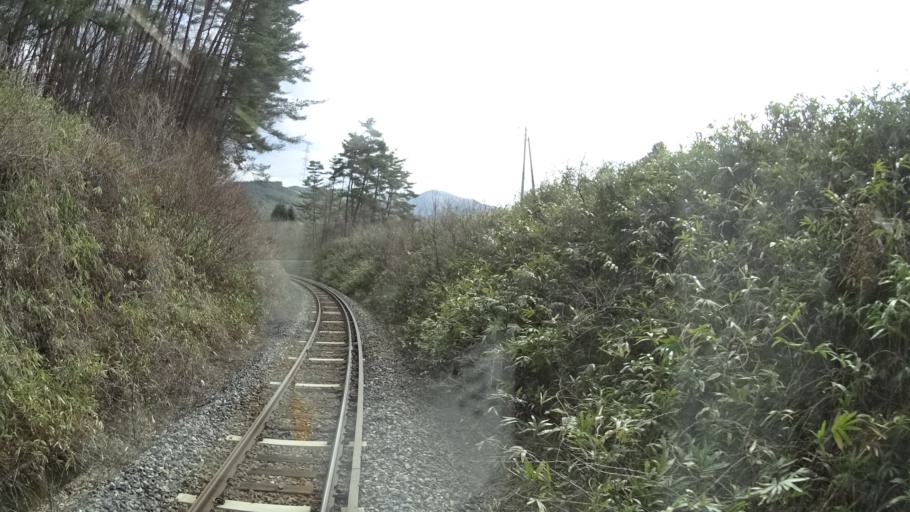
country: JP
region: Iwate
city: Tono
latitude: 39.3390
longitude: 141.3523
